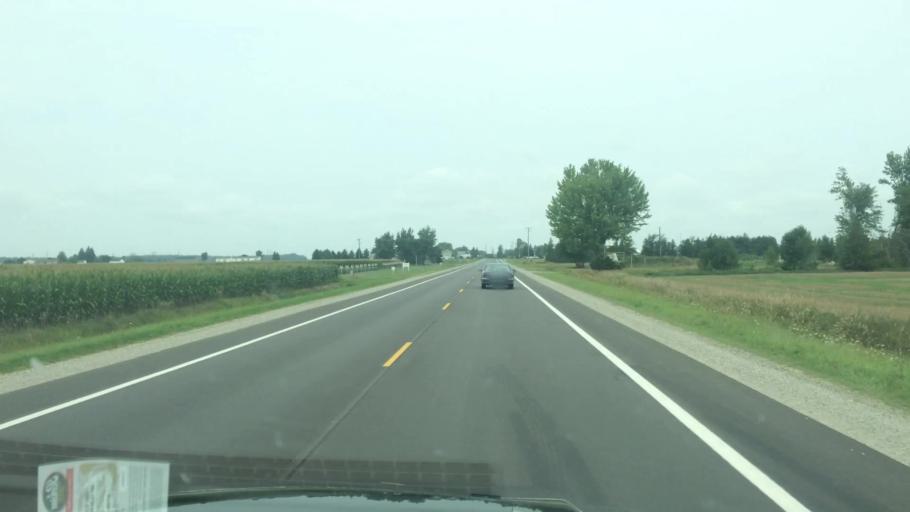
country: US
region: Michigan
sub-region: Huron County
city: Bad Axe
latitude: 43.9973
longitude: -83.0076
